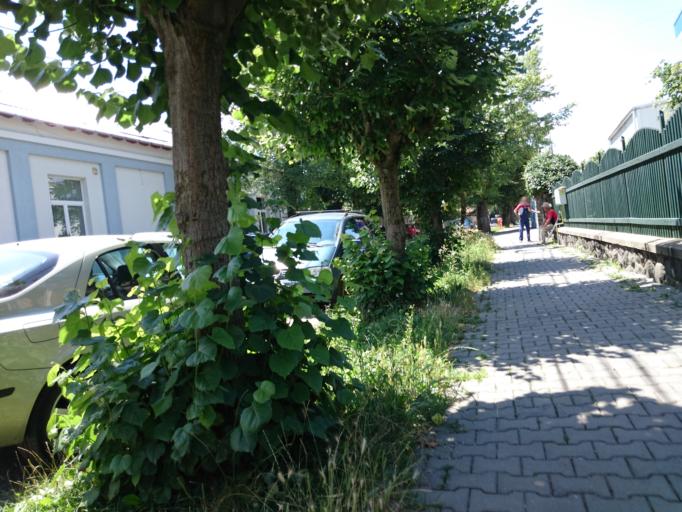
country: RO
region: Mures
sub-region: Municipiul Sighisoara
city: Sighisoara
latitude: 46.2245
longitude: 24.7971
